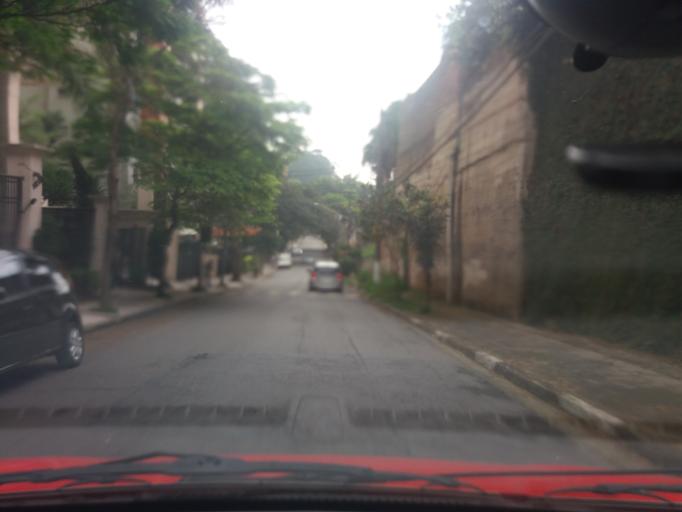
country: BR
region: Sao Paulo
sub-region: Taboao Da Serra
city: Taboao da Serra
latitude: -23.6008
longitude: -46.7254
